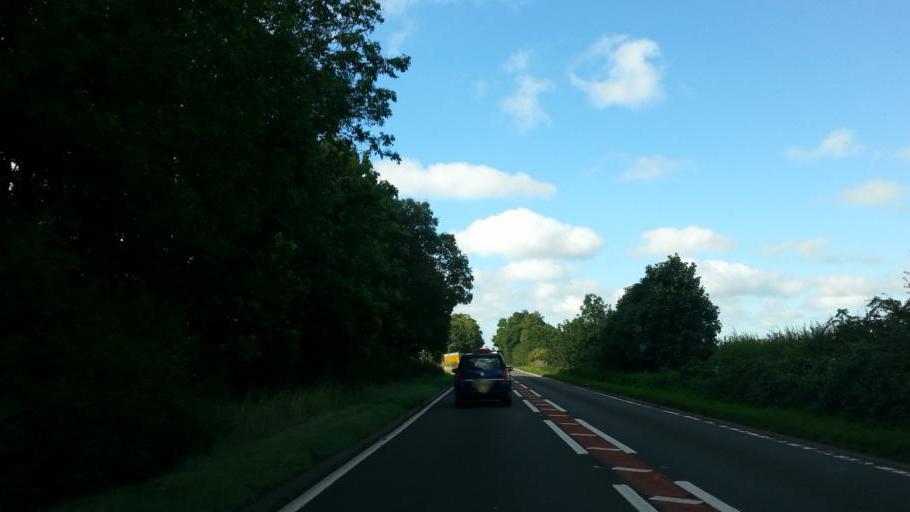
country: GB
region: England
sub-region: Northamptonshire
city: Earls Barton
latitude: 52.3065
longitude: -0.8189
